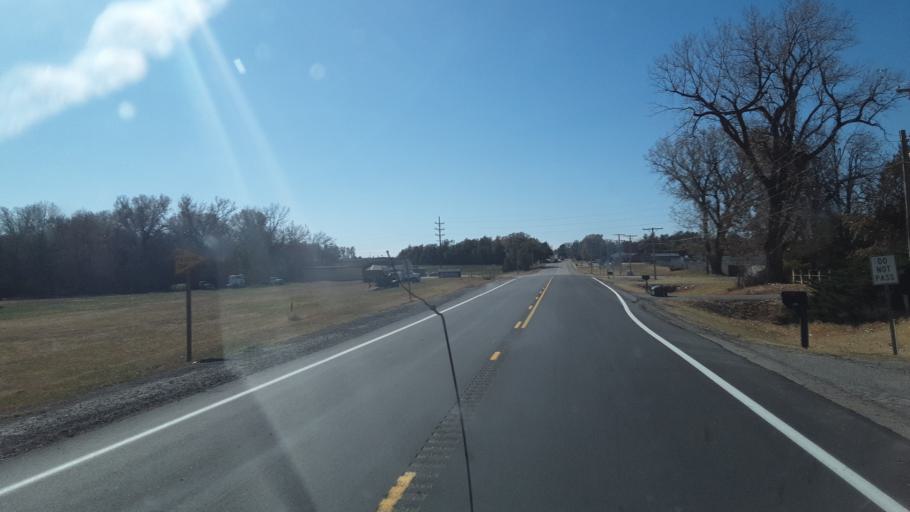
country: US
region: Kansas
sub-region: Rice County
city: Lyons
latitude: 38.3535
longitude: -98.1818
